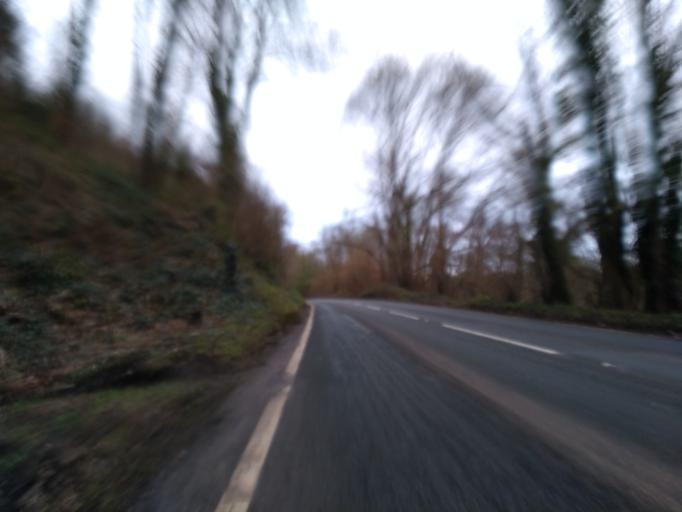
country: GB
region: England
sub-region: Devon
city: Exeter
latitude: 50.7537
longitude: -3.5318
